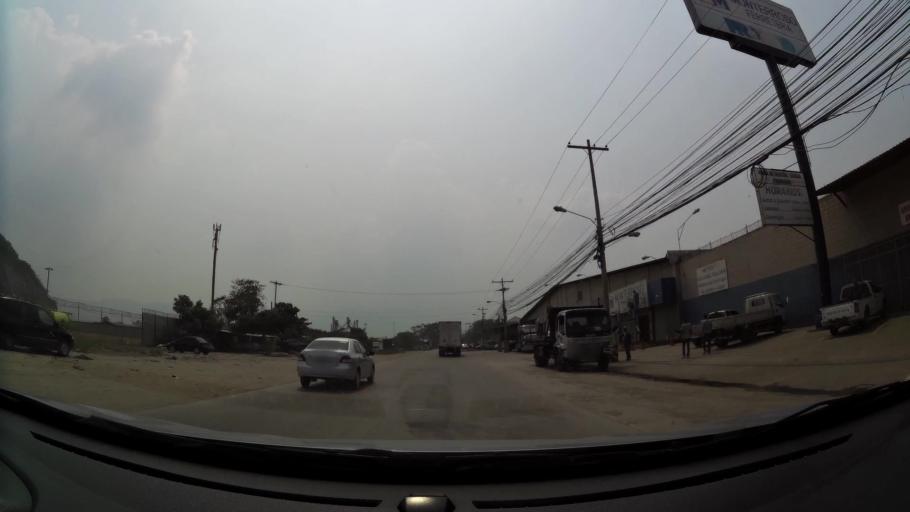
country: HN
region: Cortes
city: Chotepe
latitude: 15.4679
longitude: -87.9837
